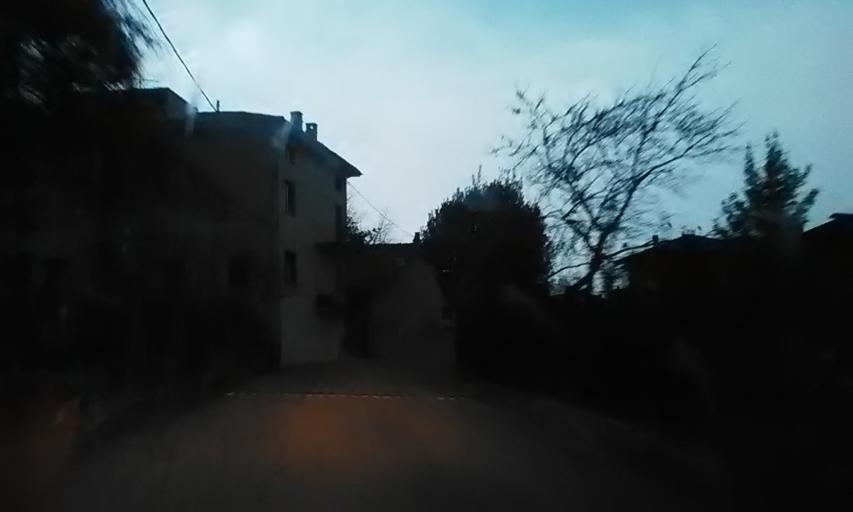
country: IT
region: Piedmont
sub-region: Provincia di Torino
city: Montalto Dora
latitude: 45.4961
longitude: 7.8637
